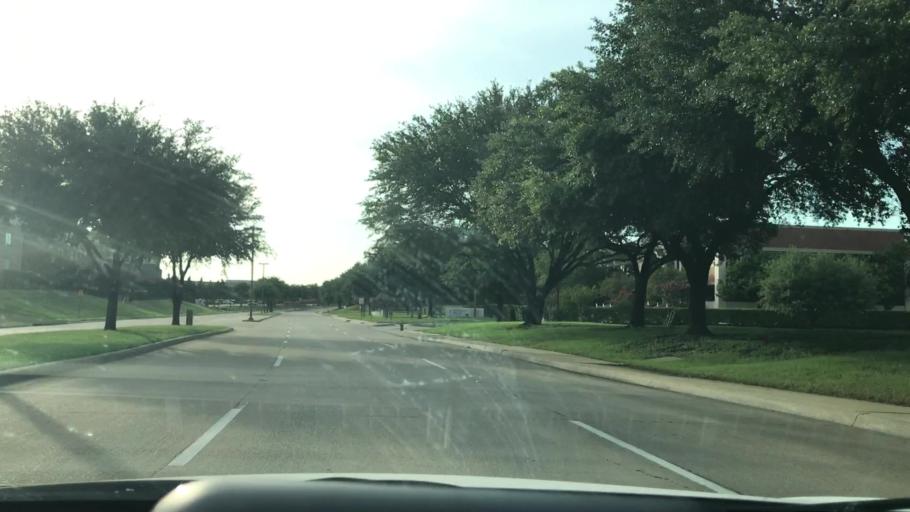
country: US
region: Texas
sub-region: Dallas County
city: Farmers Branch
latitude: 32.8919
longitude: -96.9417
